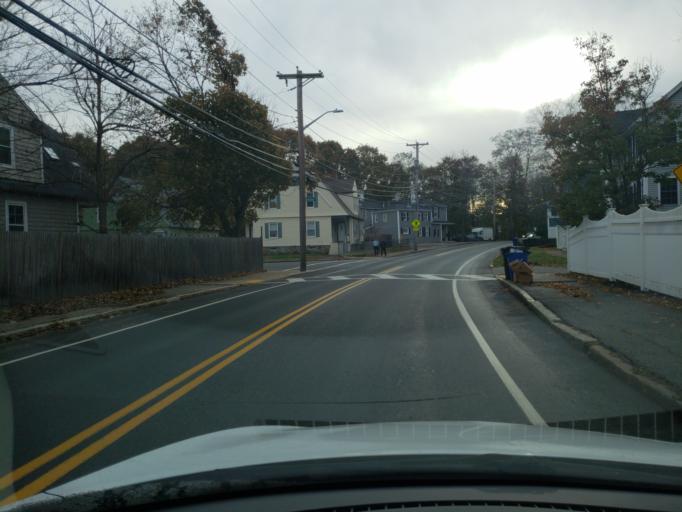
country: US
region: Massachusetts
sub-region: Essex County
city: Andover
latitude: 42.6592
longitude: -71.1490
